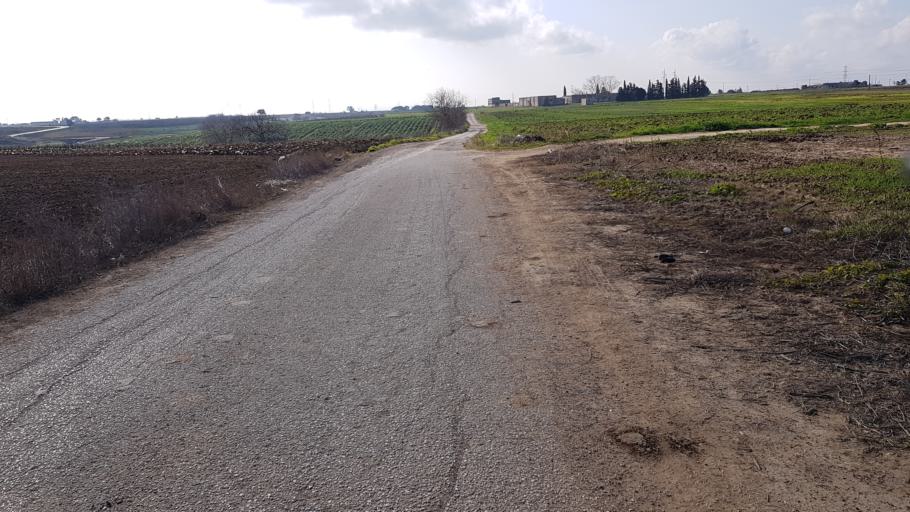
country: IT
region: Apulia
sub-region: Provincia di Brindisi
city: La Rosa
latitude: 40.5954
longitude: 17.9178
